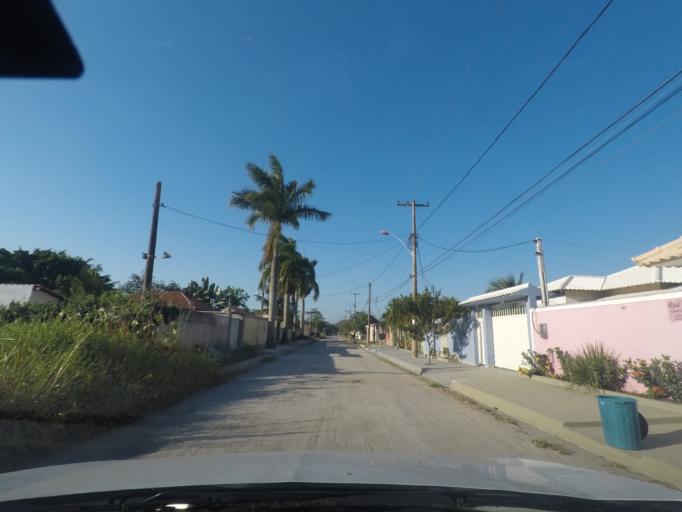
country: BR
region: Rio de Janeiro
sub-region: Marica
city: Marica
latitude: -22.9615
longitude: -42.9370
